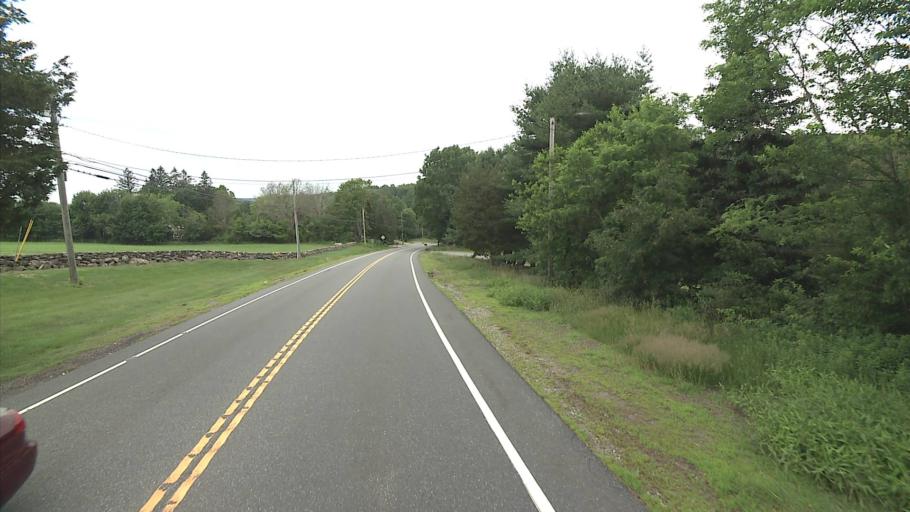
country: US
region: Connecticut
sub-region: New London County
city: Ledyard Center
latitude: 41.4686
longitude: -72.0246
